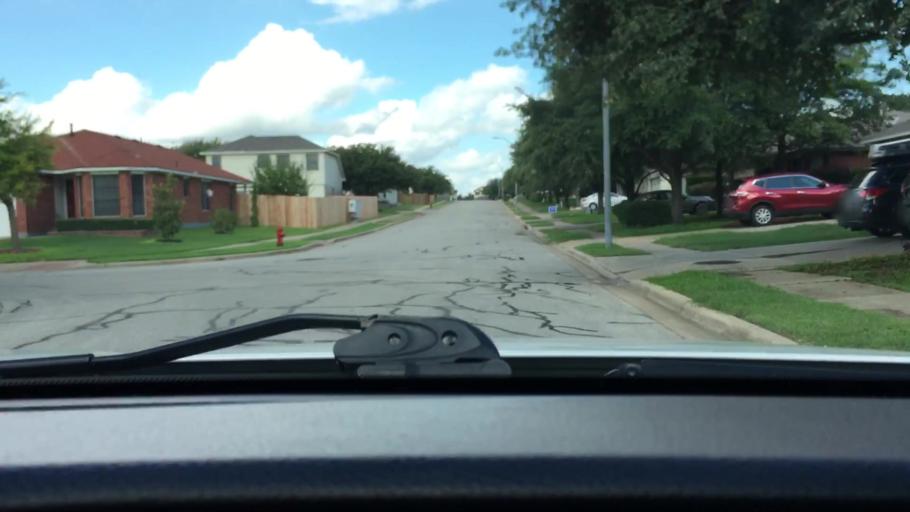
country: US
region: Texas
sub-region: Travis County
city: Windemere
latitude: 30.4740
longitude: -97.6492
